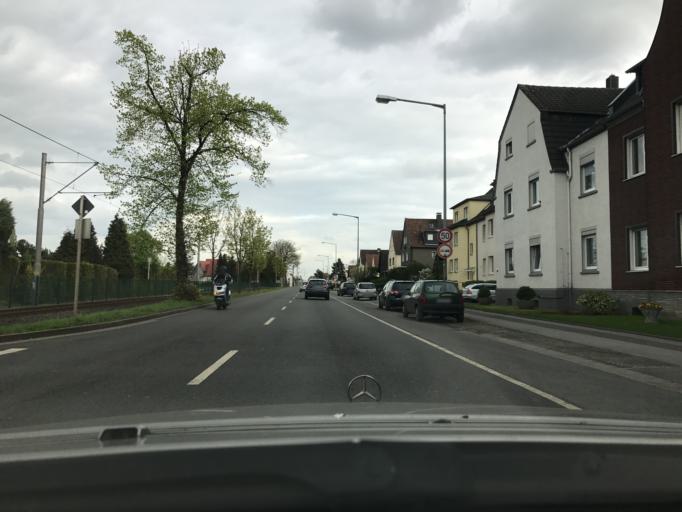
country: DE
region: North Rhine-Westphalia
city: Waltrop
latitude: 51.5836
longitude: 7.4514
